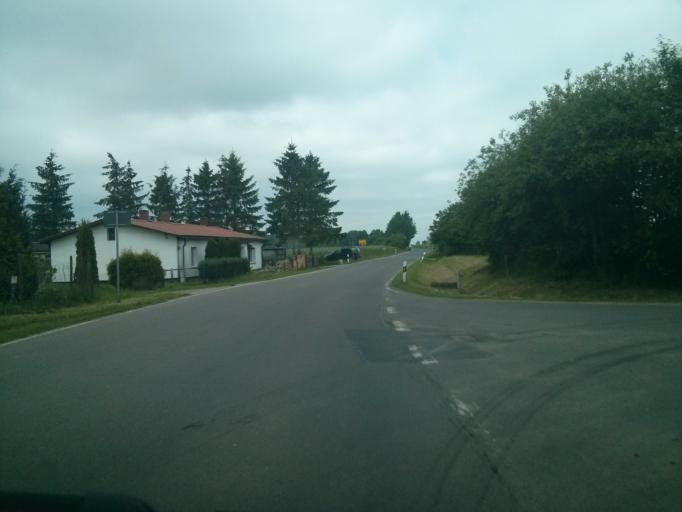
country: DE
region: Mecklenburg-Vorpommern
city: Velgast
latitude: 54.2246
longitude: 12.8324
